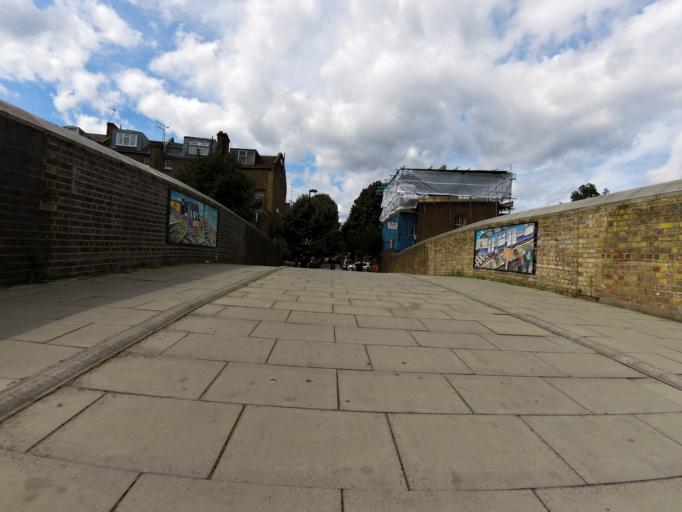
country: GB
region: England
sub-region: Greater London
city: Crouch End
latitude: 51.5672
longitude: -0.1247
